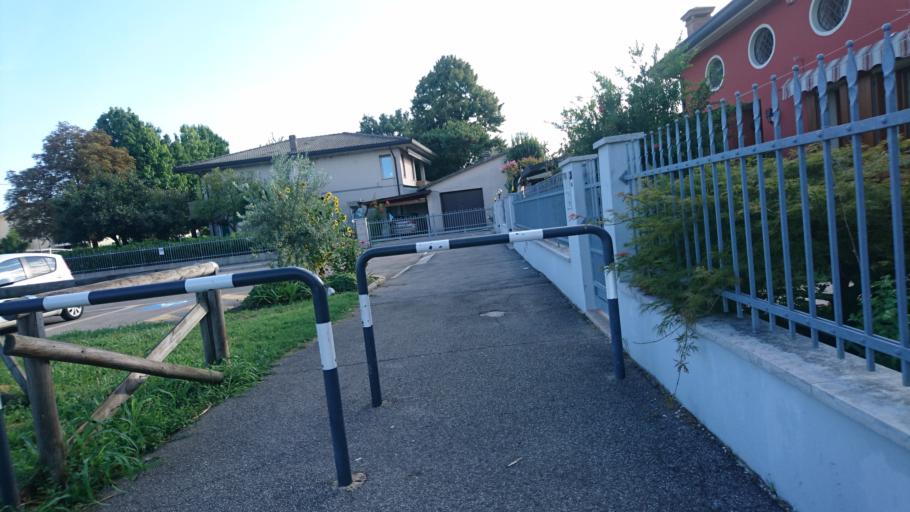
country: IT
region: Veneto
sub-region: Provincia di Padova
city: Terradura
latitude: 45.3221
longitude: 11.8212
